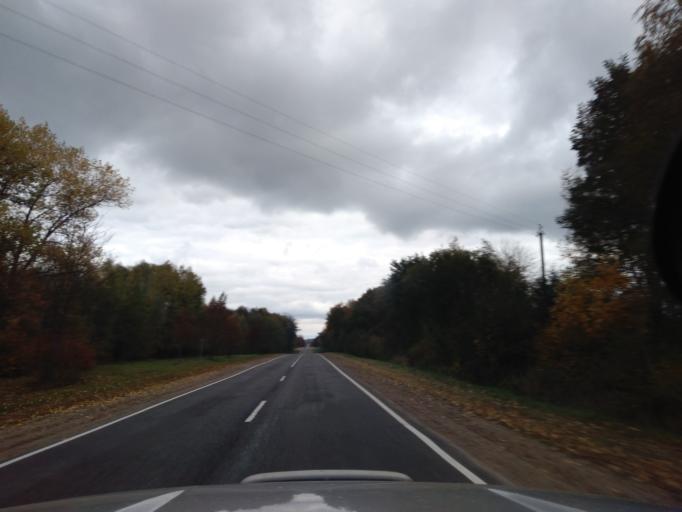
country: BY
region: Minsk
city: Slutsk
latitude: 53.2225
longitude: 27.3686
